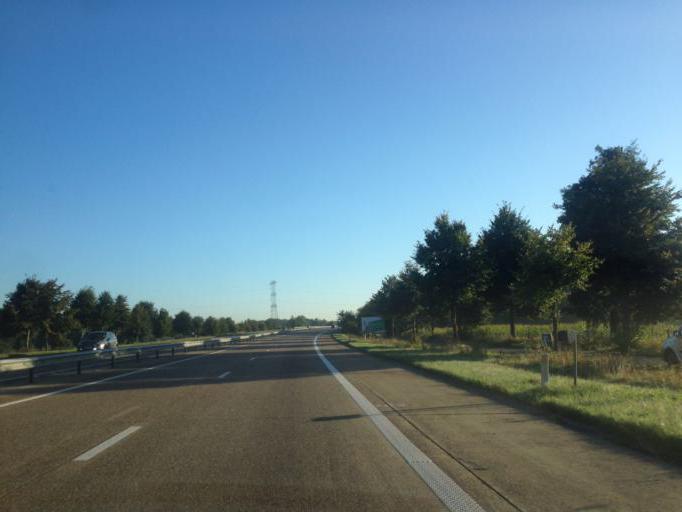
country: BE
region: Flanders
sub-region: Provincie Limburg
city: Peer
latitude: 51.1346
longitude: 5.3897
